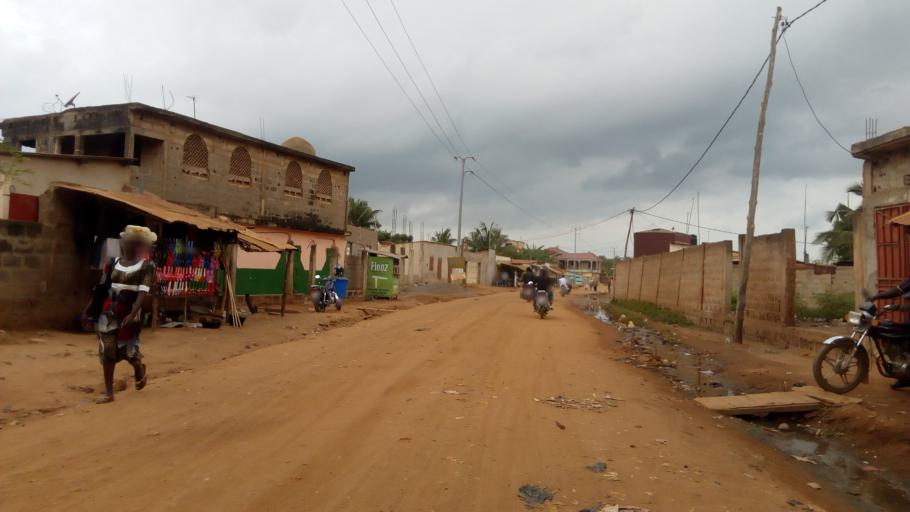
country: TG
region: Maritime
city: Lome
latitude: 6.2527
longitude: 1.2162
